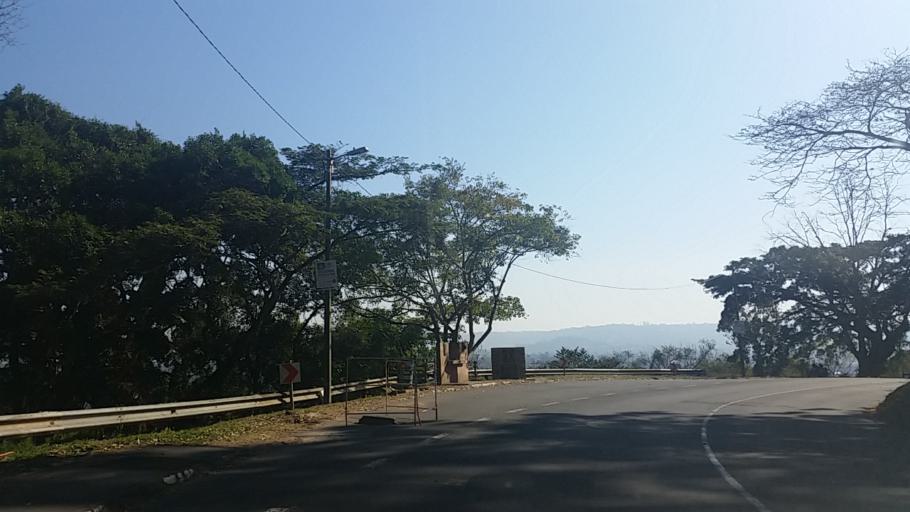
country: ZA
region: KwaZulu-Natal
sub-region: eThekwini Metropolitan Municipality
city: Berea
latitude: -29.8290
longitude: 30.8856
